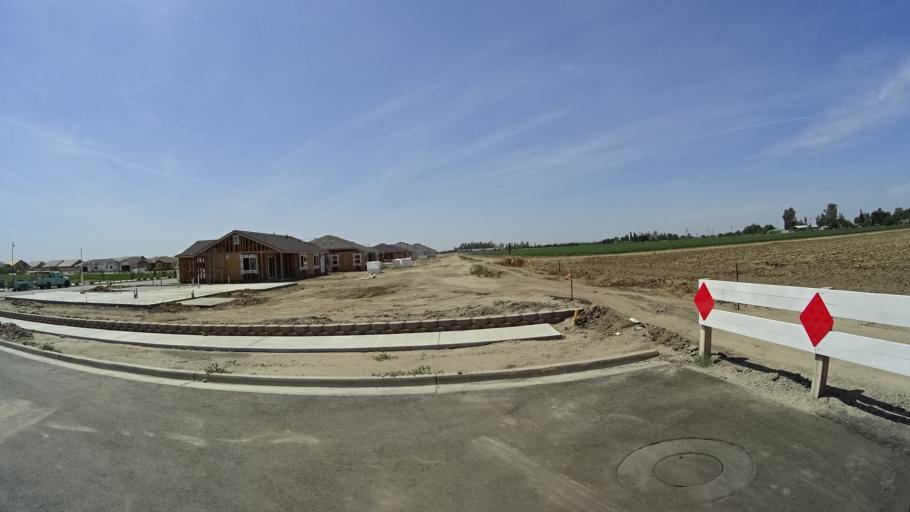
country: US
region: California
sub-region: Kings County
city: Lucerne
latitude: 36.3539
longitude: -119.6865
